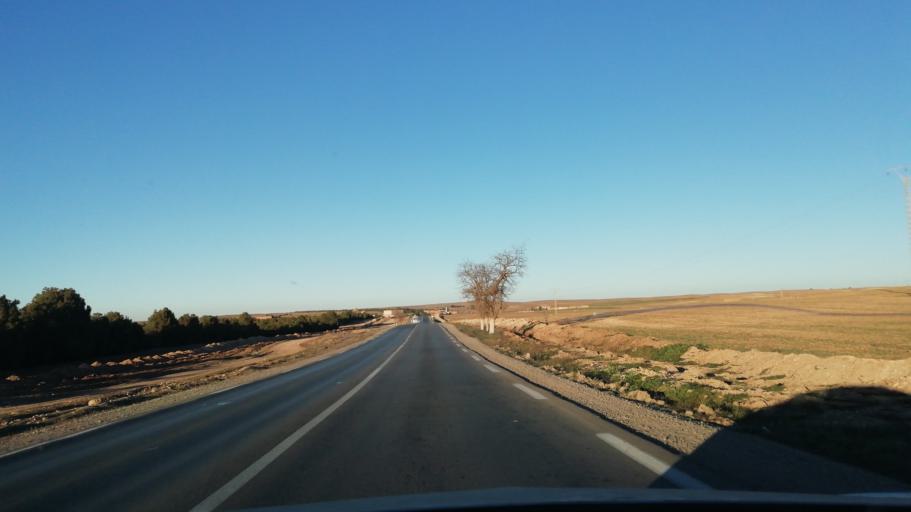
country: DZ
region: Saida
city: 'Ain el Hadjar
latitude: 34.5691
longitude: 0.1235
